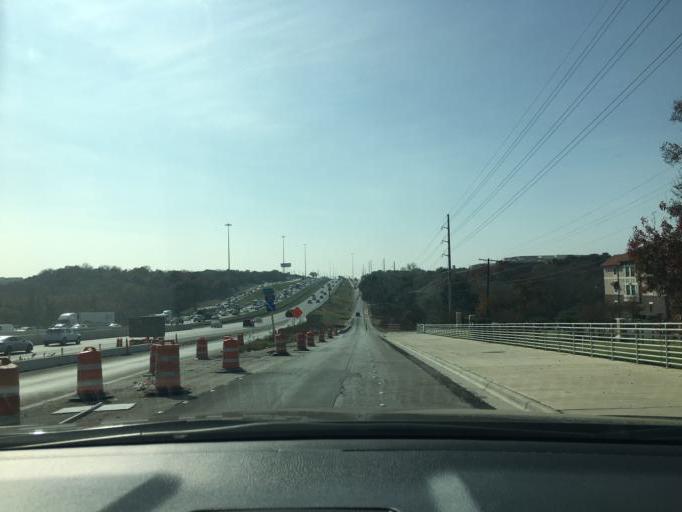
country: US
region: Texas
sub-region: Travis County
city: Onion Creek
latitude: 30.1818
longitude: -97.7768
